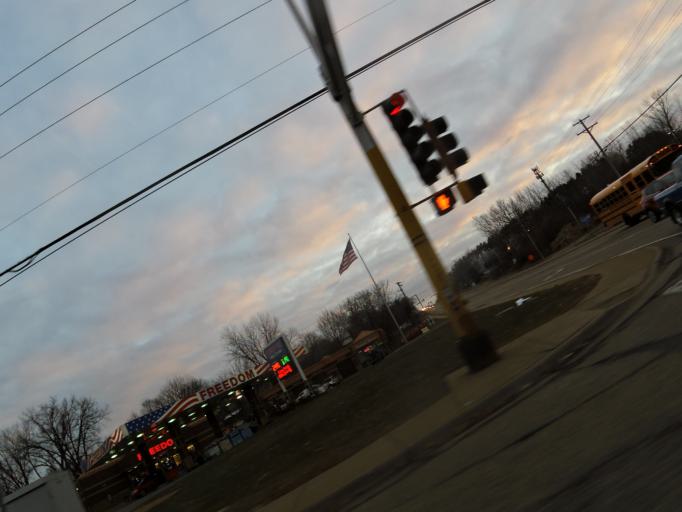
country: US
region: Minnesota
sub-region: Washington County
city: Birchwood
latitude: 45.0502
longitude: -92.9846
